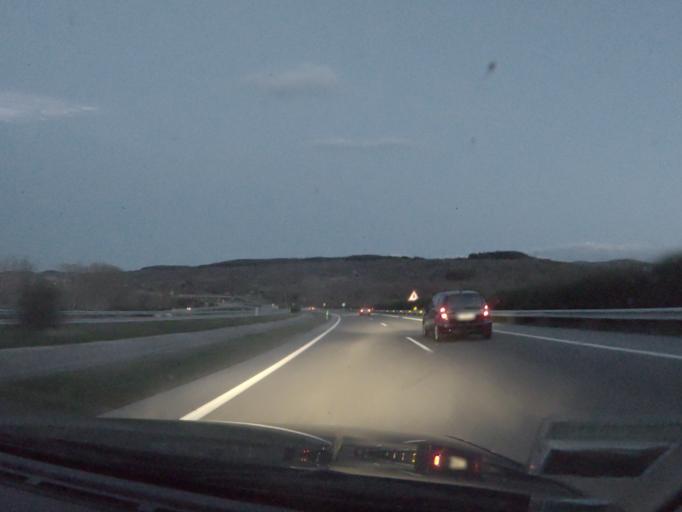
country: ES
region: Castille and Leon
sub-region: Provincia de Leon
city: Torre del Bierzo
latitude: 42.6039
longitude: -6.3815
